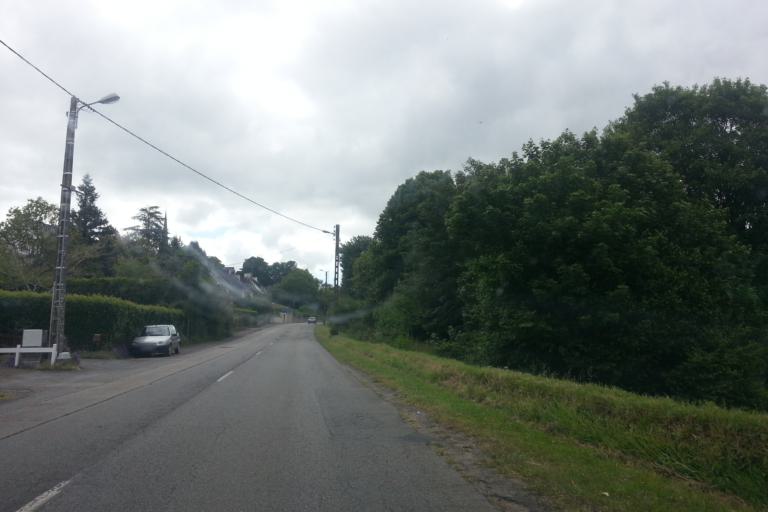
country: FR
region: Brittany
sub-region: Departement du Finistere
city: Elliant
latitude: 47.9940
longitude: -3.8967
